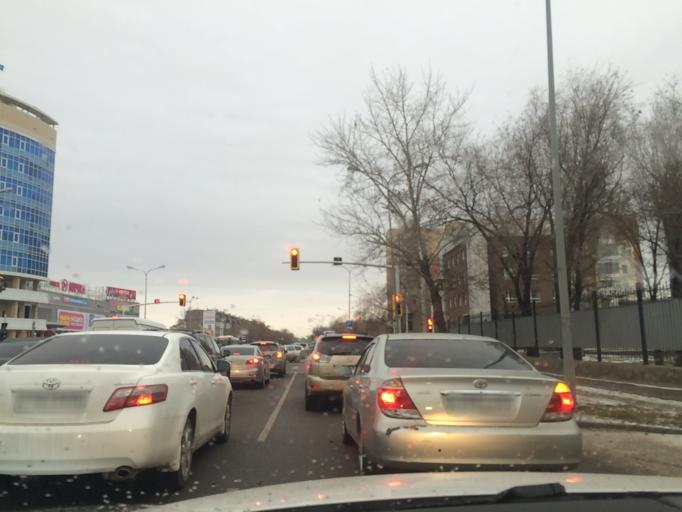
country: KZ
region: Astana Qalasy
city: Astana
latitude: 51.1739
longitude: 71.4251
